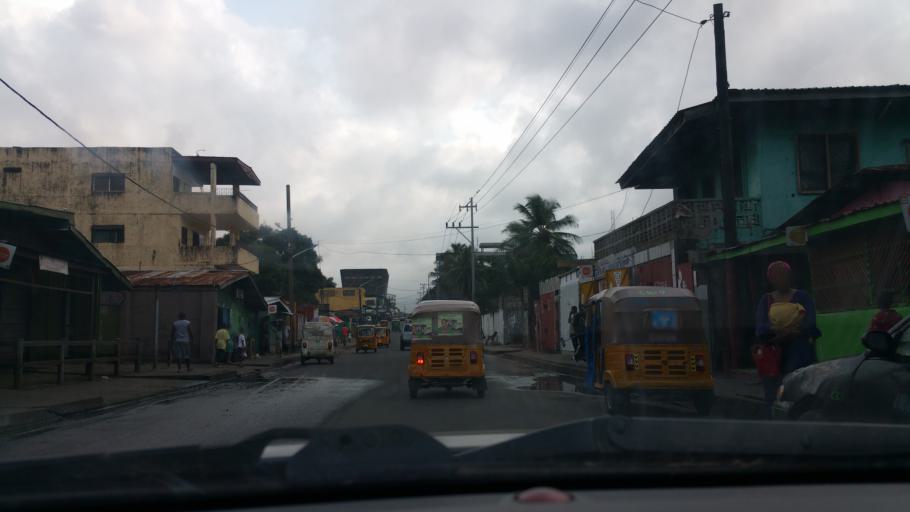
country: LR
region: Montserrado
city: Monrovia
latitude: 6.3139
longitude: -10.8102
